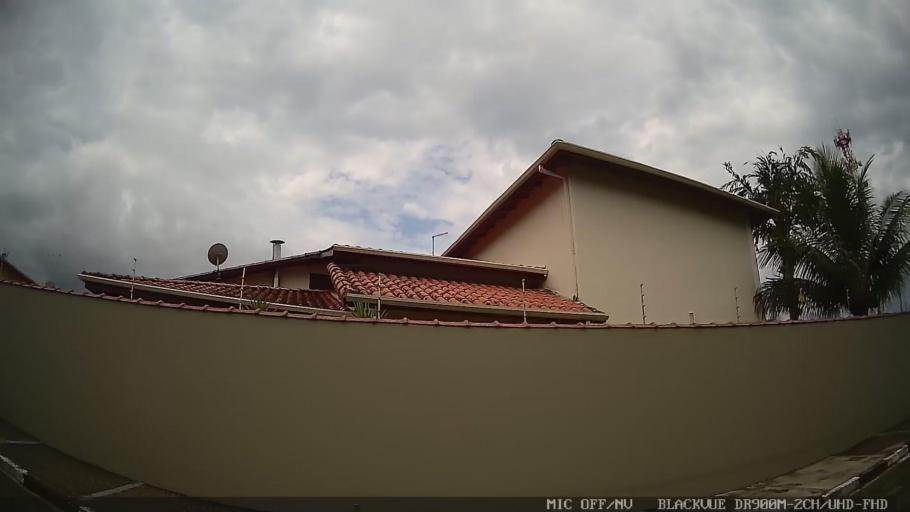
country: BR
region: Sao Paulo
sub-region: Caraguatatuba
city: Caraguatatuba
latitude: -23.6266
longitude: -45.4200
